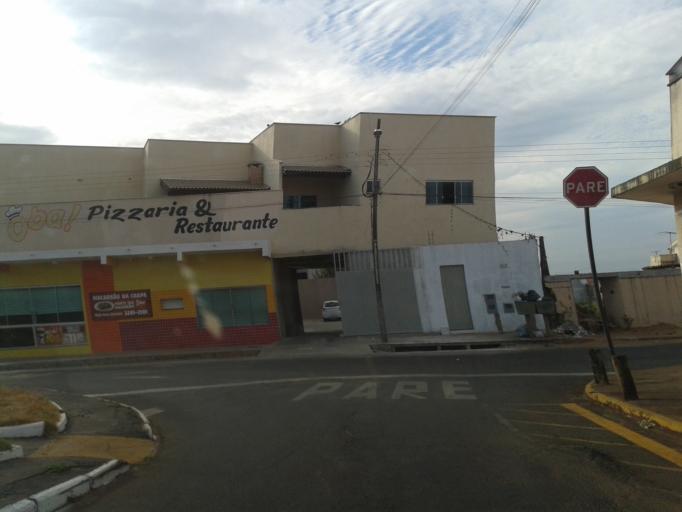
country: BR
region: Minas Gerais
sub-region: Ituiutaba
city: Ituiutaba
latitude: -18.9837
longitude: -49.4510
